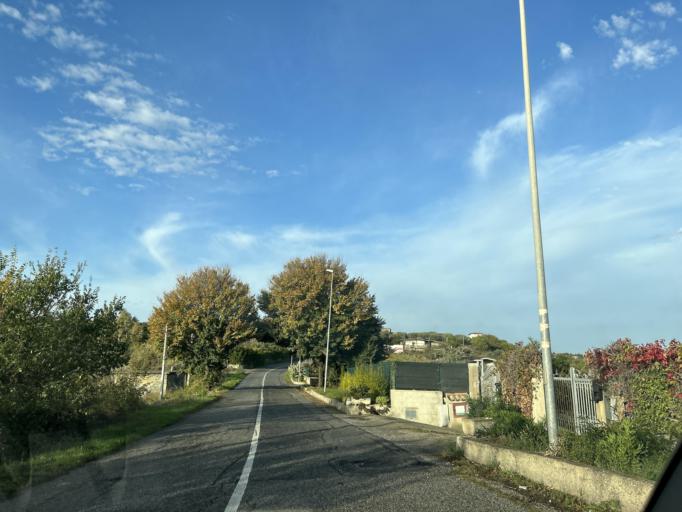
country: IT
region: Calabria
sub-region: Provincia di Catanzaro
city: Staletti
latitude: 38.7666
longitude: 16.5298
